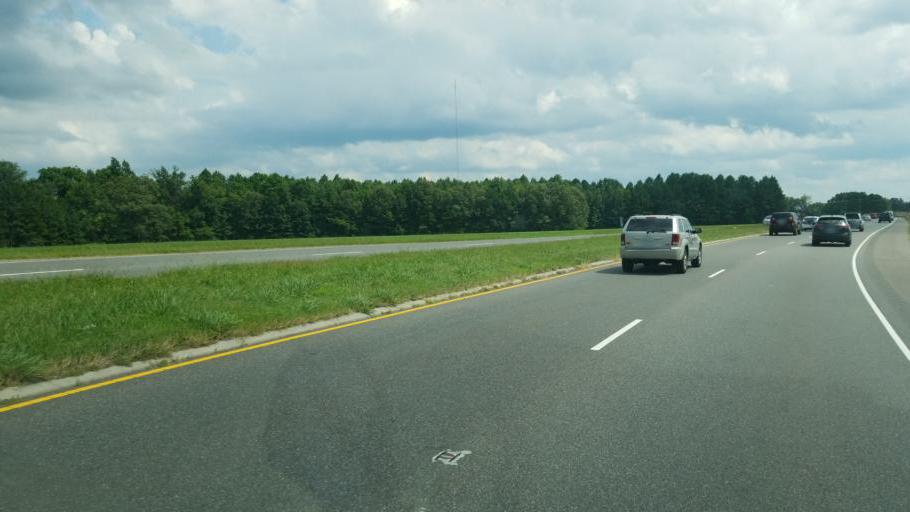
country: US
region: North Carolina
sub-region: Currituck County
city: Moyock
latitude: 36.5597
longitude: -76.1967
